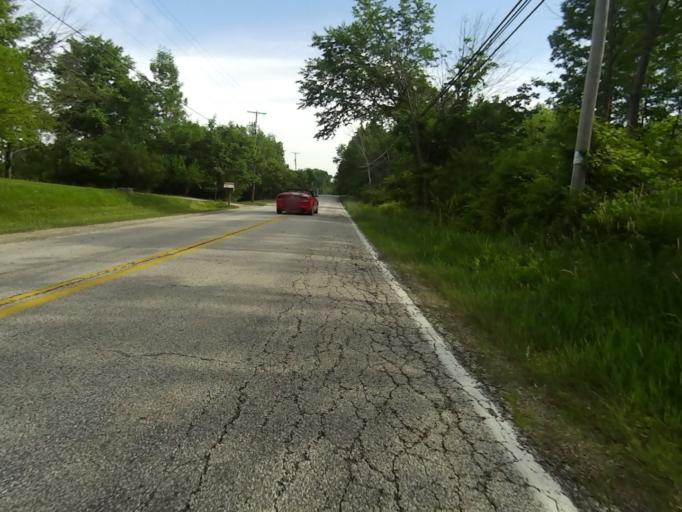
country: US
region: Ohio
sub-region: Portage County
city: Kent
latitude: 41.1802
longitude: -81.3658
